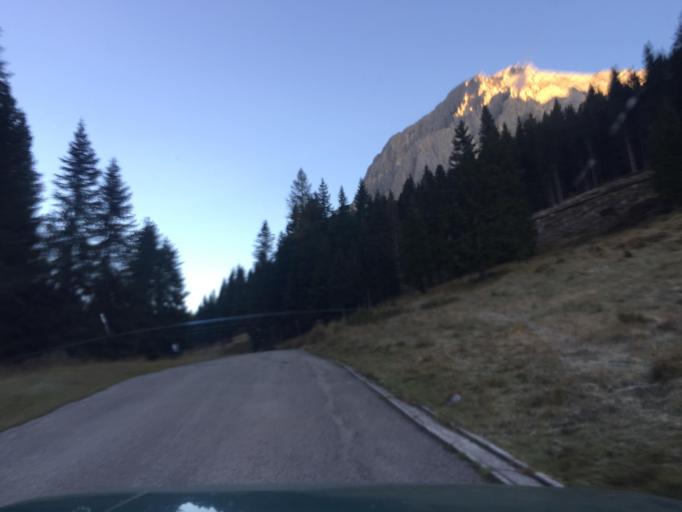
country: IT
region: Veneto
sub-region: Provincia di Belluno
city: Granvilla
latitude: 46.6131
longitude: 12.7206
